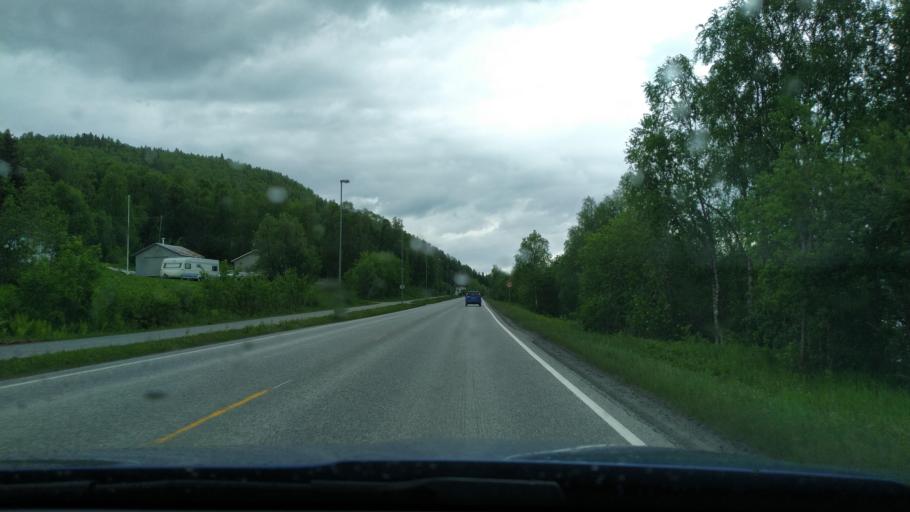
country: NO
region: Troms
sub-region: Malselv
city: Moen
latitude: 69.0198
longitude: 18.4874
